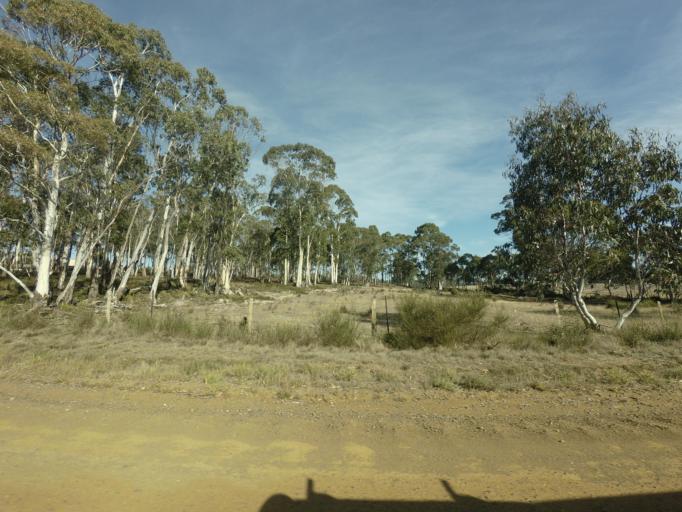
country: AU
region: Tasmania
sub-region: Sorell
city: Sorell
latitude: -42.4726
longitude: 147.4675
